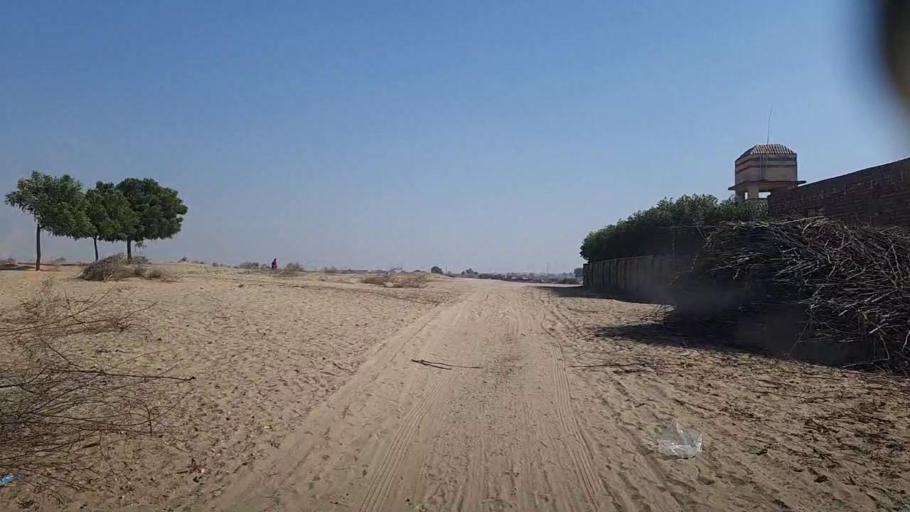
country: PK
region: Sindh
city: Khairpur
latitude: 28.0027
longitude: 69.8570
